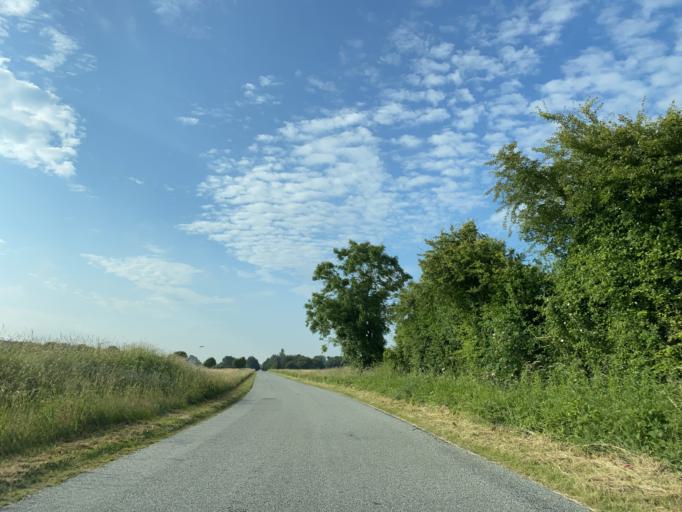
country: DK
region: South Denmark
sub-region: Haderslev Kommune
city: Haderslev
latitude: 55.1879
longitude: 9.4760
